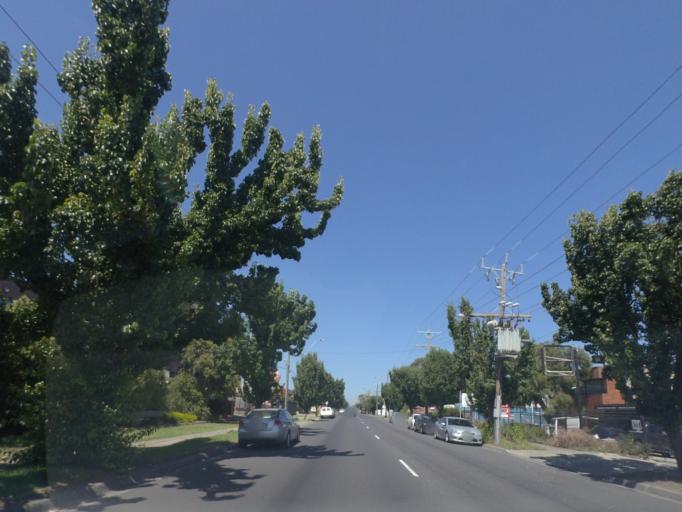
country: AU
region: Victoria
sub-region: Whittlesea
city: Thomastown
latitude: -37.6885
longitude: 145.0185
